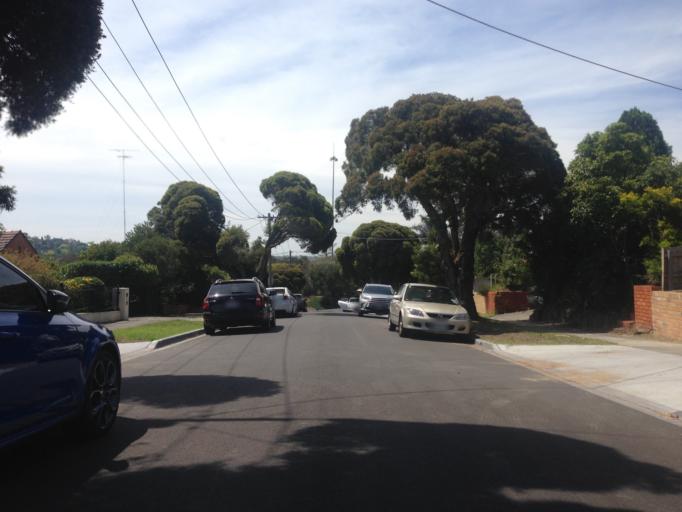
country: AU
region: Victoria
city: Ivanhoe East
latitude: -37.7847
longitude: 145.0711
